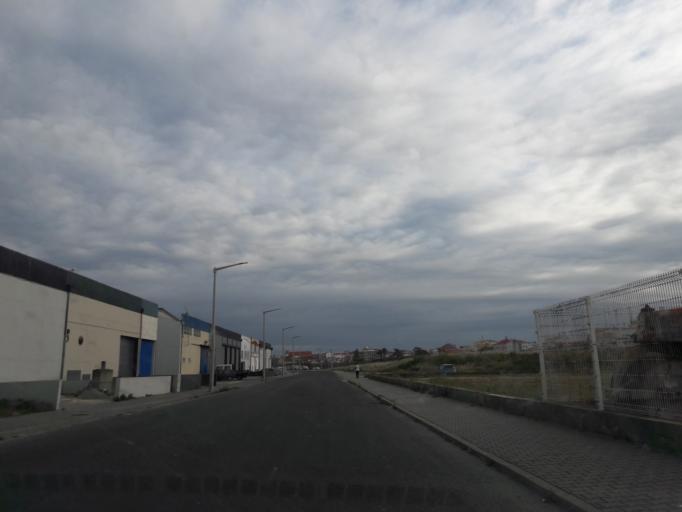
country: PT
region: Leiria
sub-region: Peniche
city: Peniche
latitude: 39.3627
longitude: -9.3754
